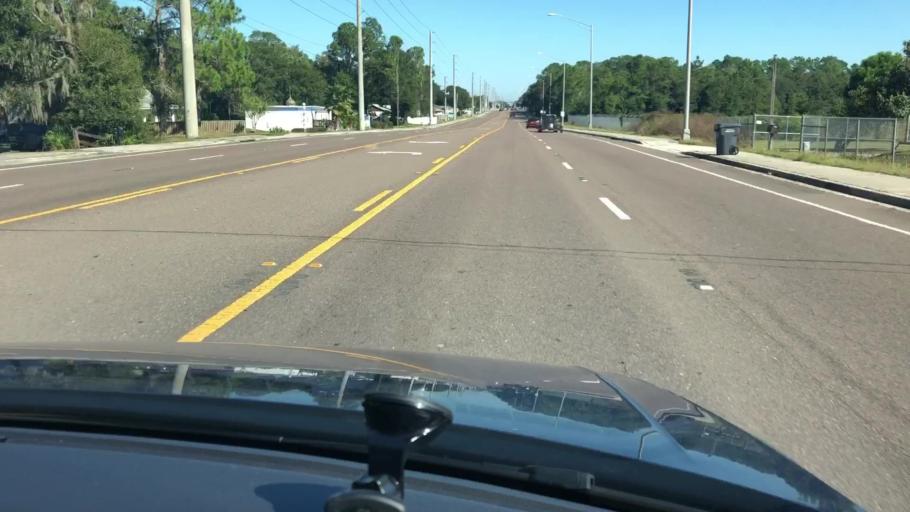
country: US
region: Florida
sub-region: Polk County
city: Gibsonia
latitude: 28.1281
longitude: -81.9633
